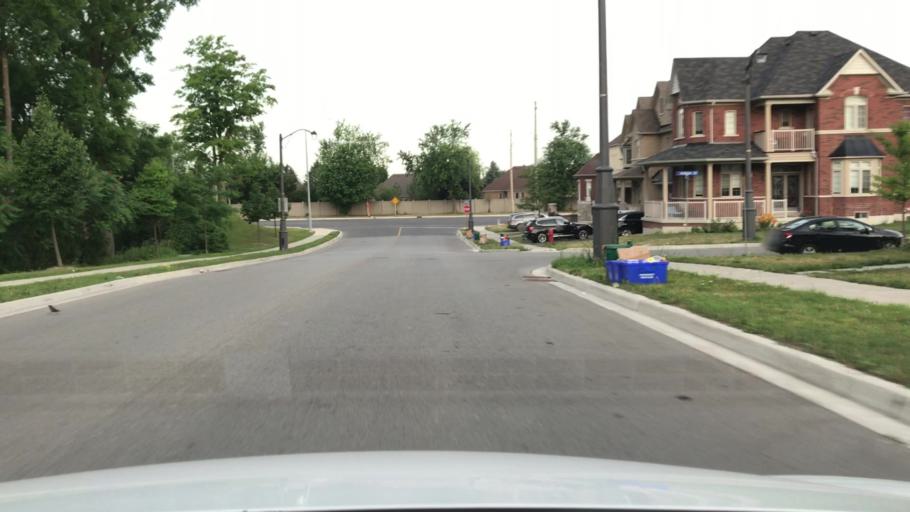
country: CA
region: Ontario
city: Newmarket
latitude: 44.0358
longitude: -79.4231
